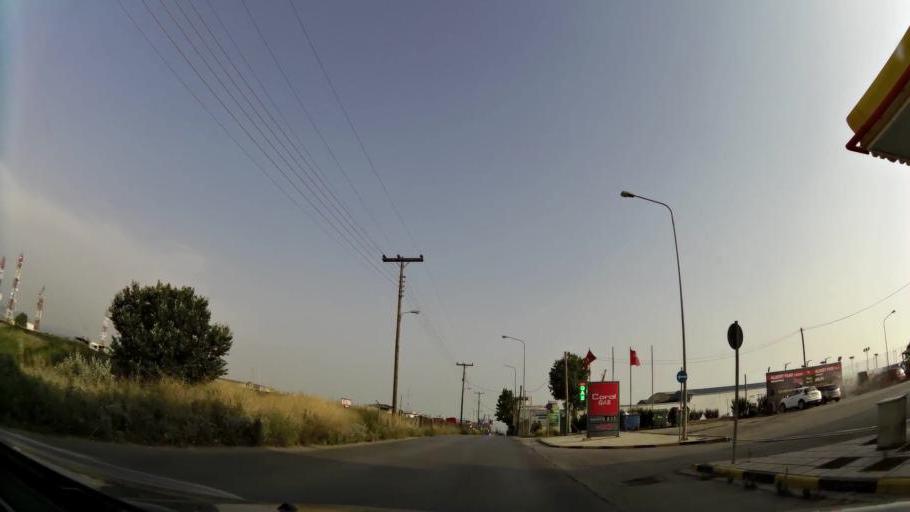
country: GR
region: Central Macedonia
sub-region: Nomos Thessalonikis
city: Evosmos
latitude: 40.6896
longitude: 22.9060
